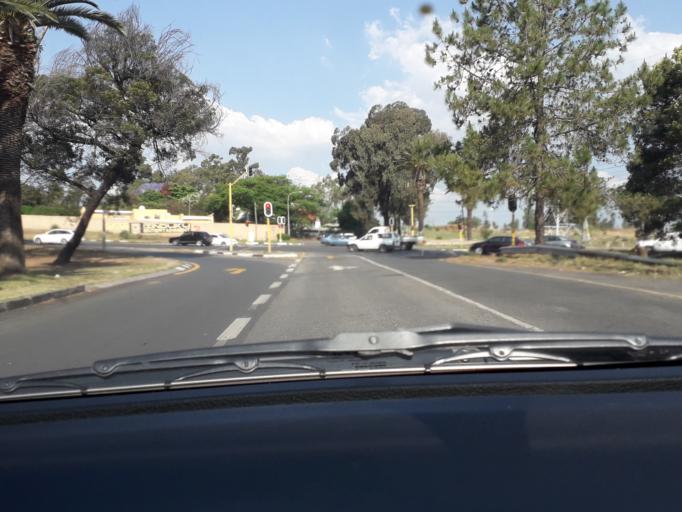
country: ZA
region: Gauteng
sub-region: City of Johannesburg Metropolitan Municipality
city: Modderfontein
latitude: -26.1260
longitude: 28.1322
